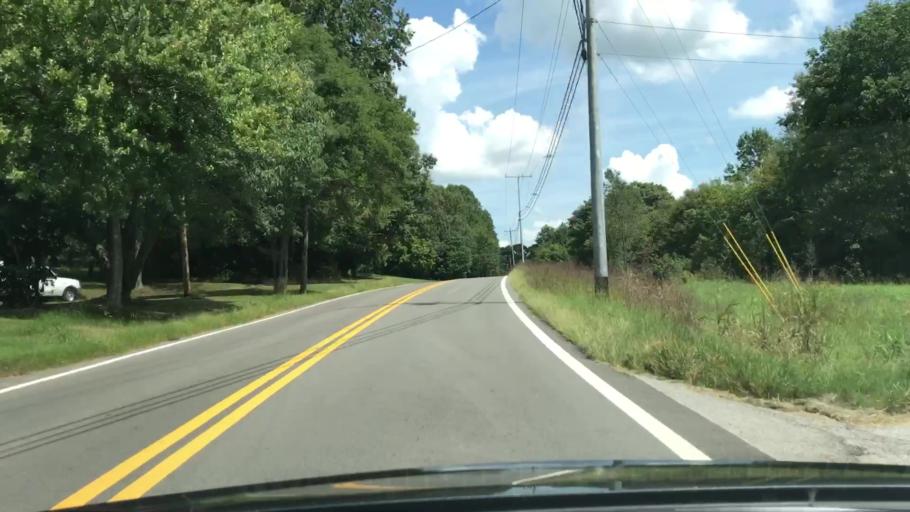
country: US
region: Tennessee
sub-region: Sumner County
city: Portland
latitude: 36.5310
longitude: -86.5408
